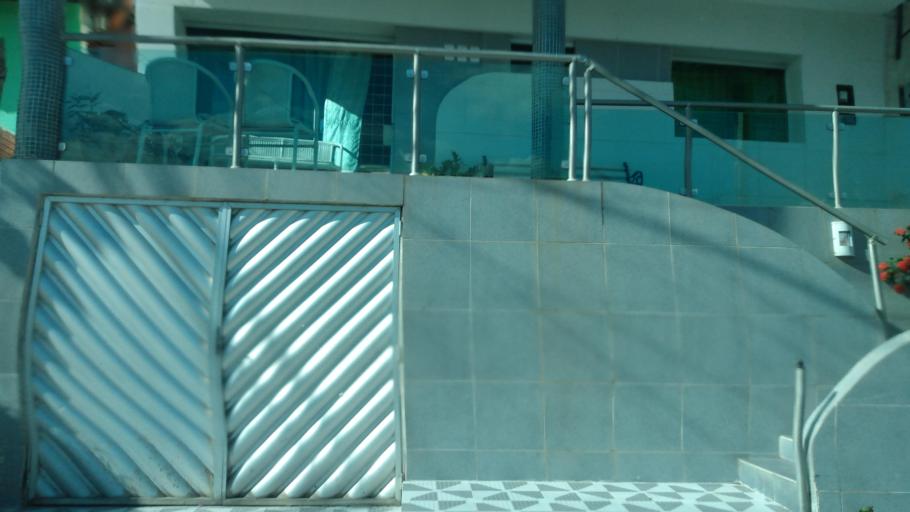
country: ET
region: Oromiya
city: Gore
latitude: 8.2004
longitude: 35.5671
